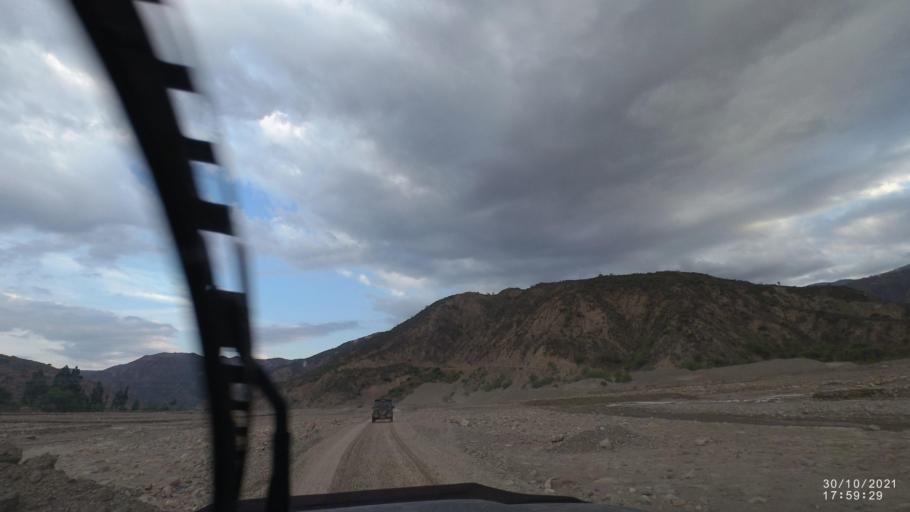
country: BO
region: Cochabamba
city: Sipe Sipe
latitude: -17.5543
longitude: -66.4728
